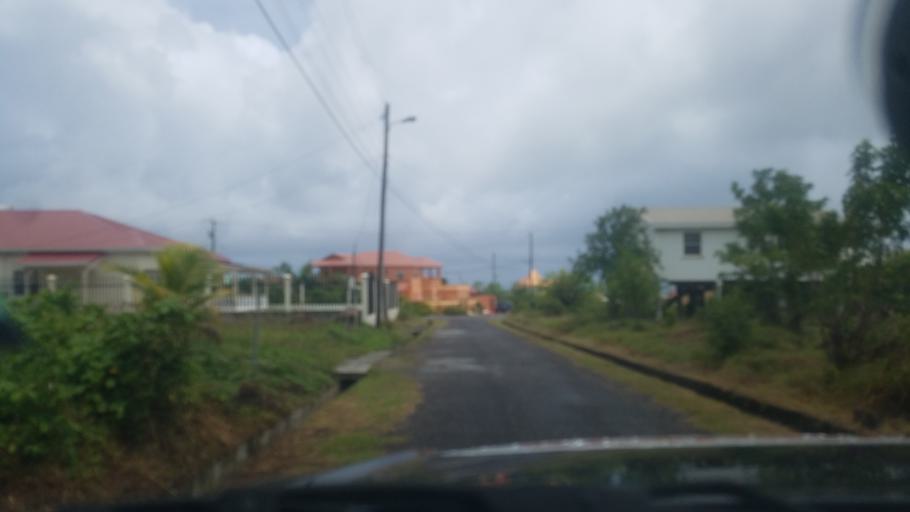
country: LC
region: Laborie Quarter
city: Laborie
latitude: 13.7494
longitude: -60.9757
